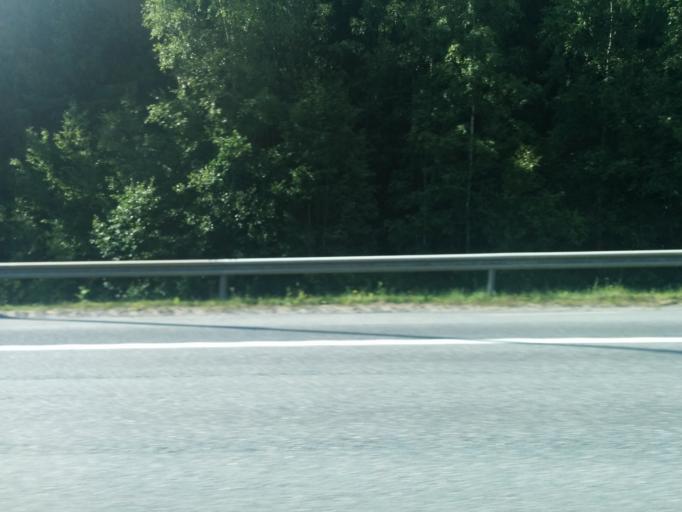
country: FI
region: Pirkanmaa
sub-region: Tampere
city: Tampere
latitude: 61.5064
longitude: 23.9023
